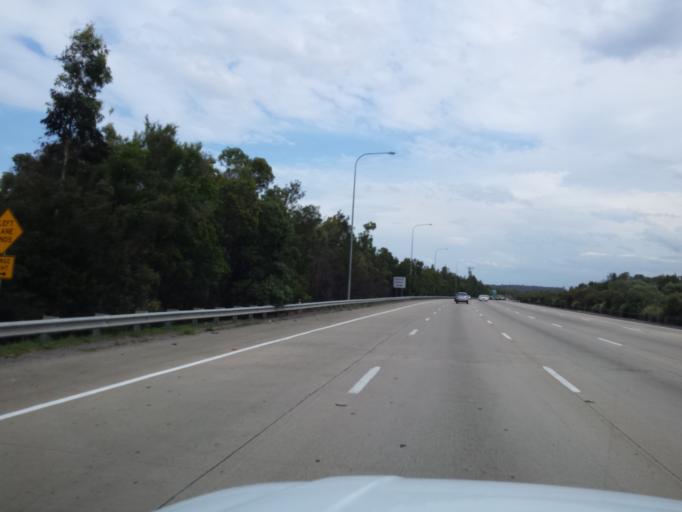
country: AU
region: Queensland
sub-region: Gold Coast
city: Oxenford
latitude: -27.9312
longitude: 153.3337
